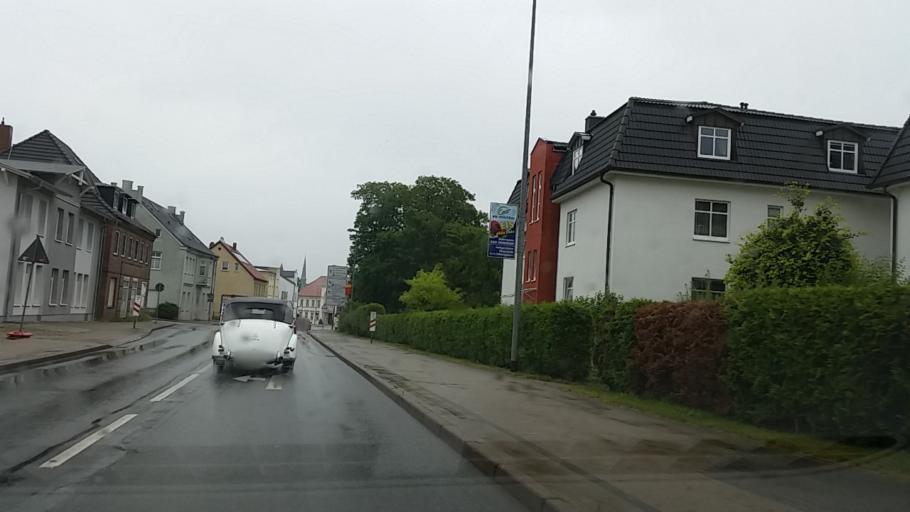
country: DE
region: Mecklenburg-Vorpommern
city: Bad Doberan
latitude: 54.1023
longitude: 11.9003
